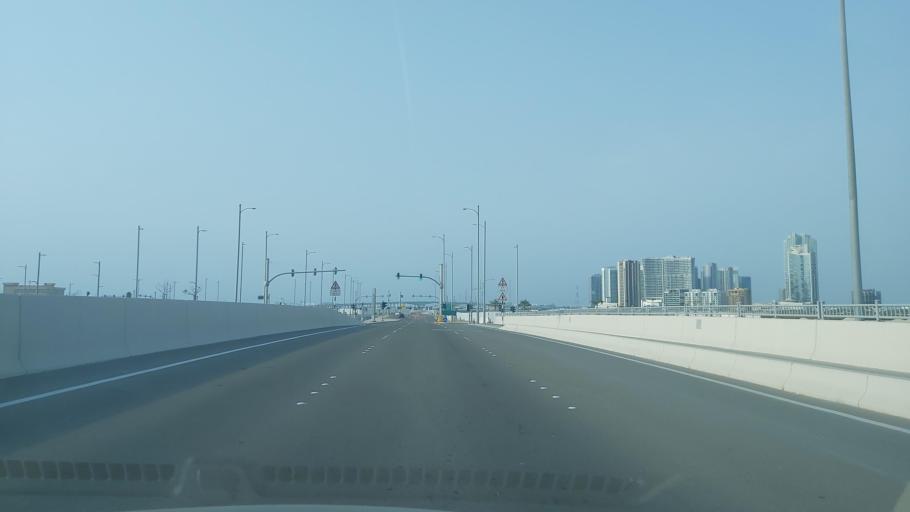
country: AE
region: Abu Dhabi
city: Abu Dhabi
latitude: 24.4955
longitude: 54.3984
